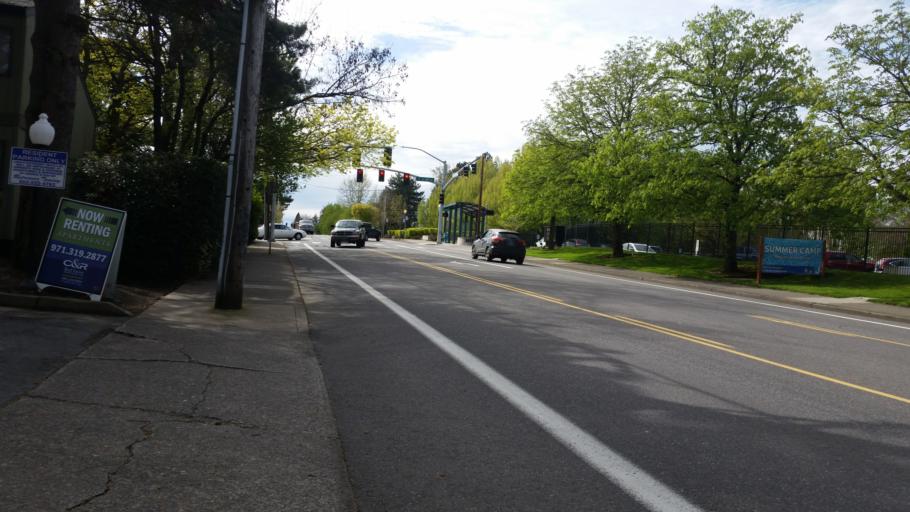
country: US
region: Oregon
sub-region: Multnomah County
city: Portland
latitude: 45.4760
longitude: -122.7031
